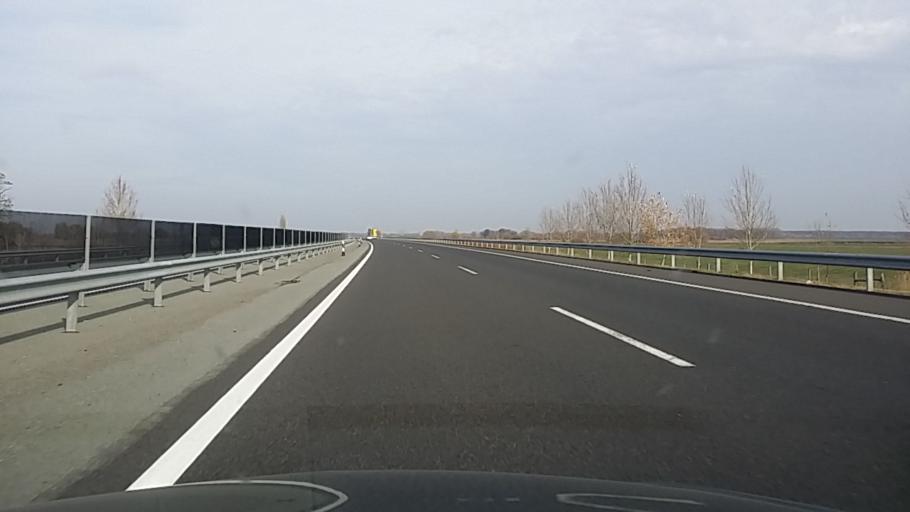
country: HU
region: Hajdu-Bihar
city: Gorbehaza
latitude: 47.8009
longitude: 21.2906
